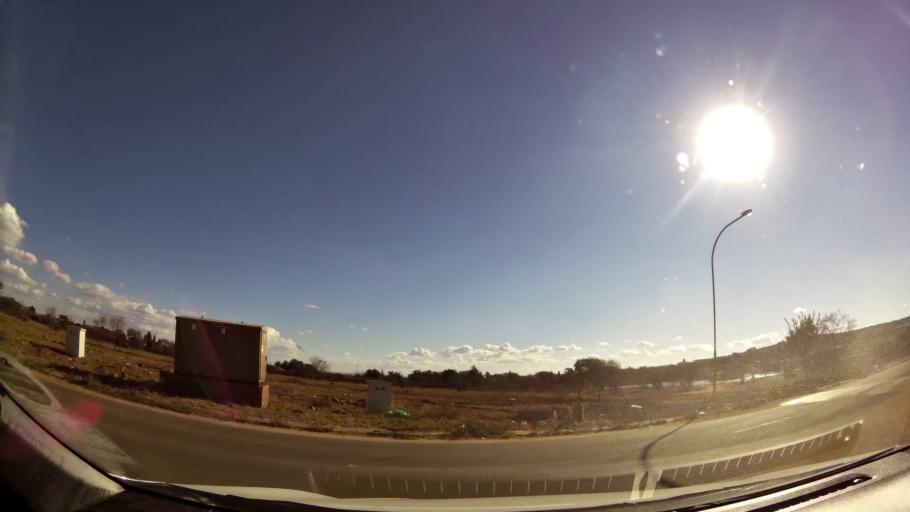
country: ZA
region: Limpopo
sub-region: Capricorn District Municipality
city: Polokwane
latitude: -23.9050
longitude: 29.5022
